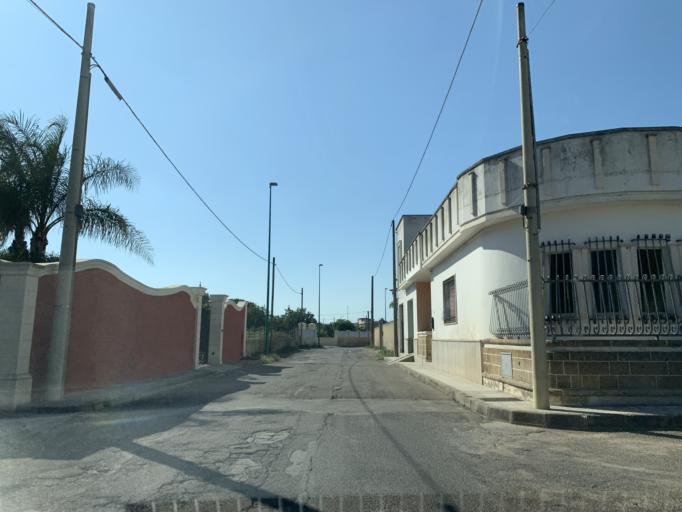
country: IT
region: Apulia
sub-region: Provincia di Lecce
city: Copertino
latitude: 40.2672
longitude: 18.0367
